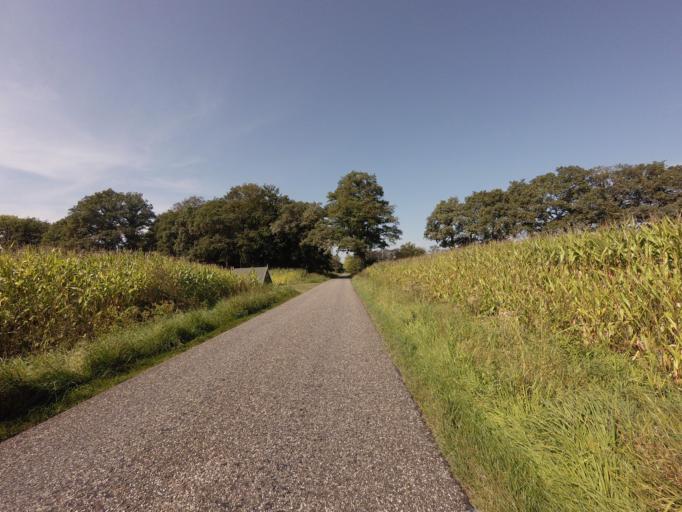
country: NL
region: Overijssel
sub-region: Gemeente Haaksbergen
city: Haaksbergen
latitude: 52.2077
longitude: 6.7674
